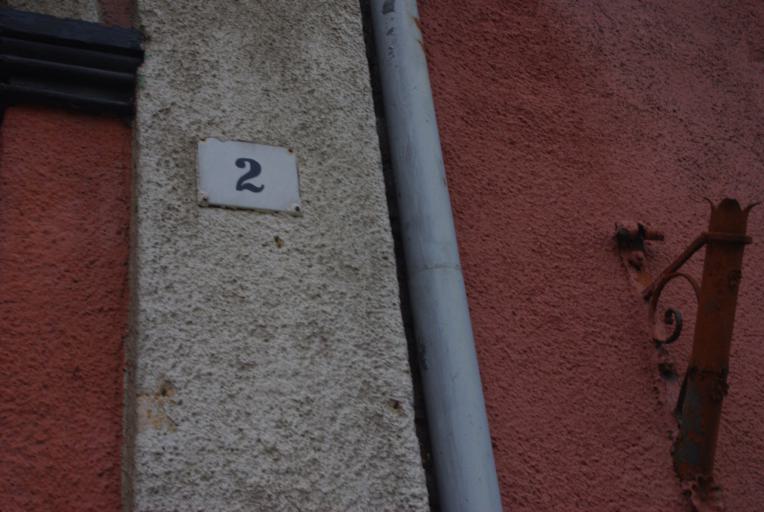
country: HU
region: Borsod-Abauj-Zemplen
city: Satoraljaujhely
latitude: 48.3932
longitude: 21.6560
